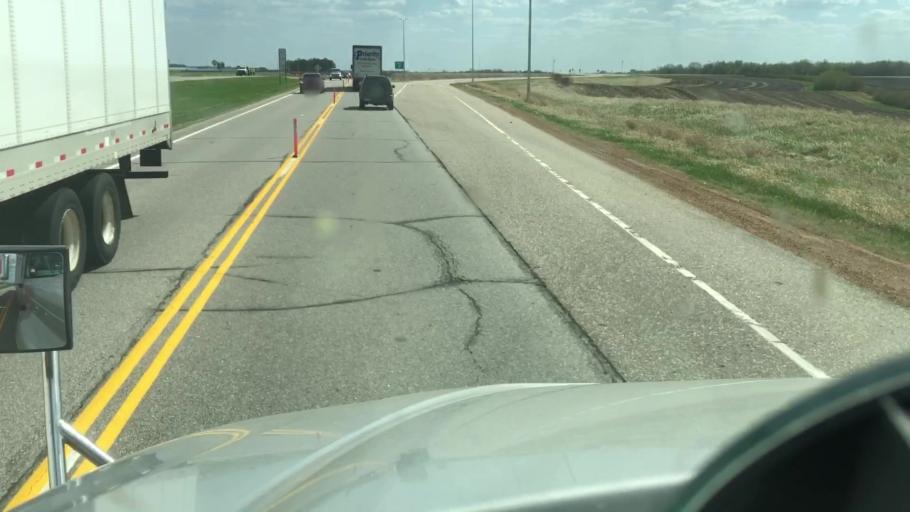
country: US
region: Minnesota
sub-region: Scott County
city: Belle Plaine
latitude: 44.5491
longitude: -93.8496
